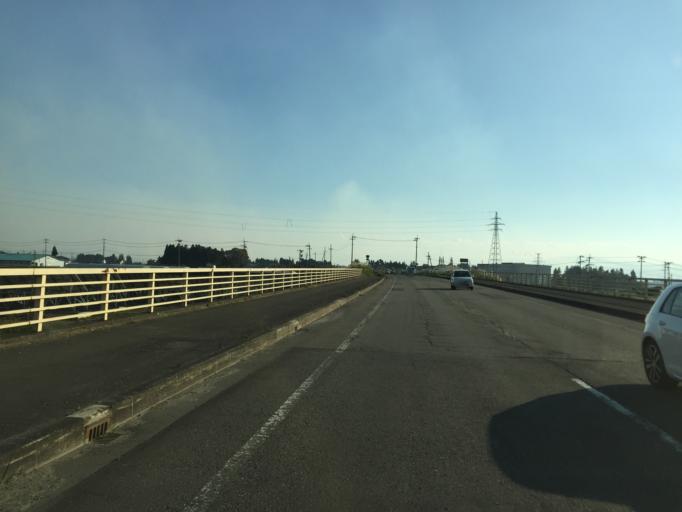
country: JP
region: Fukushima
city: Kitakata
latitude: 37.6779
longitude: 139.8881
